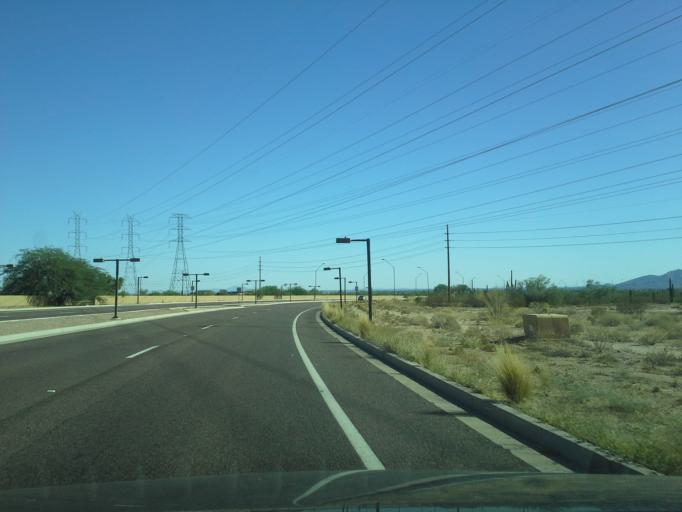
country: US
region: Arizona
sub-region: Maricopa County
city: Paradise Valley
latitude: 33.6681
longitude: -111.9048
